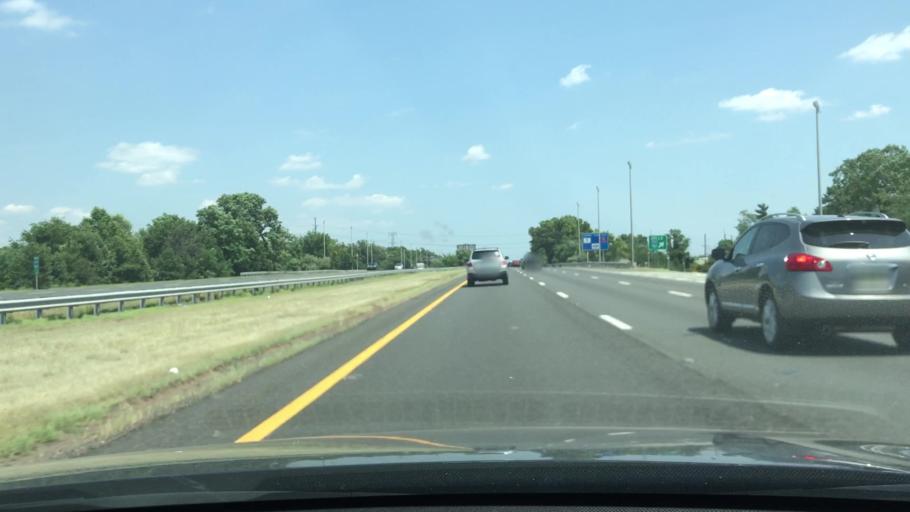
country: US
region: New Jersey
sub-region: Middlesex County
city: Society Hill
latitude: 40.5567
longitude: -74.4654
